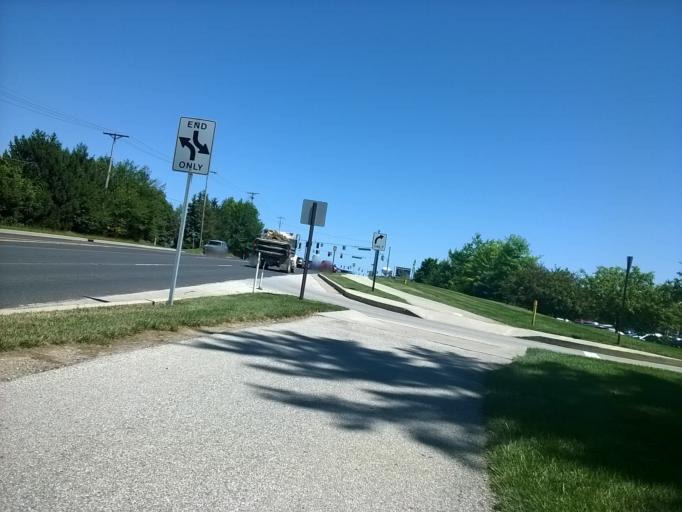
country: US
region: Indiana
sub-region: Hamilton County
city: Carmel
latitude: 39.9999
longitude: -86.1318
